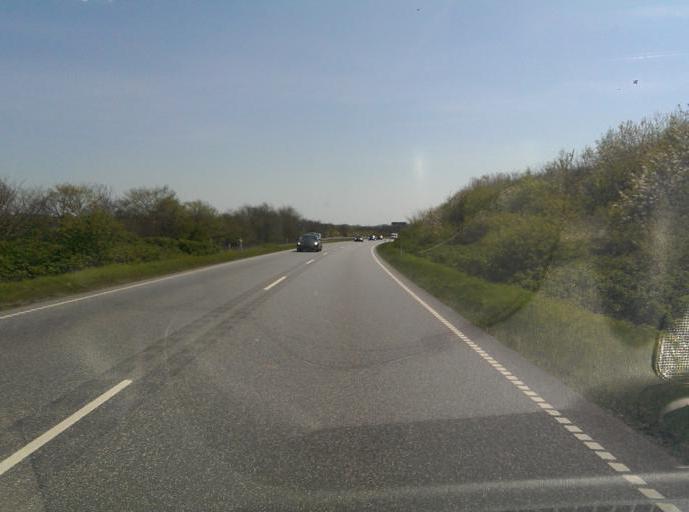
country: DK
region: South Denmark
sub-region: Esbjerg Kommune
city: Bramming
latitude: 55.4215
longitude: 8.6997
